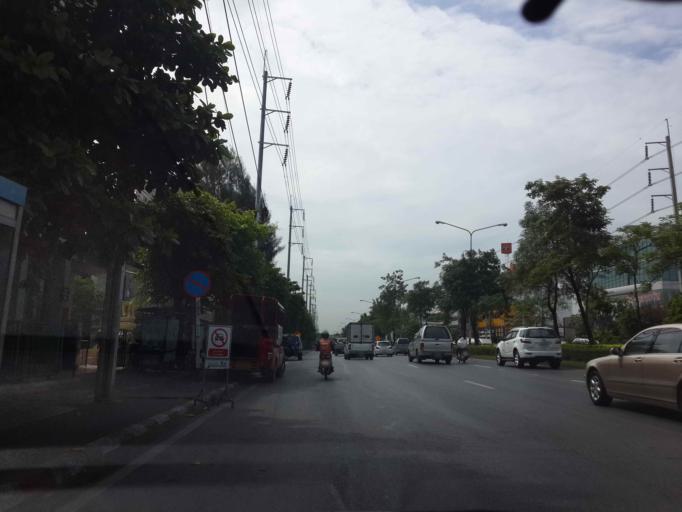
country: TH
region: Bangkok
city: Bang Khen
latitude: 13.8577
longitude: 100.6276
